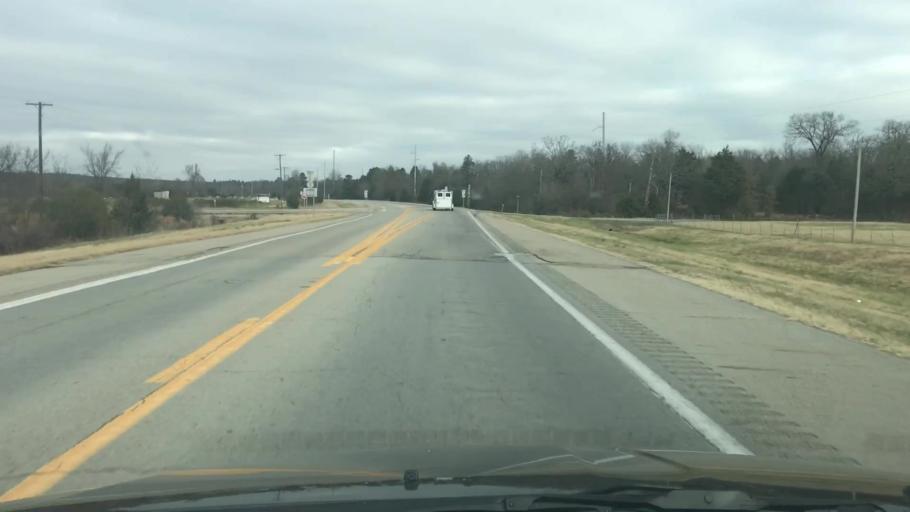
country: US
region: Arkansas
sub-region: Scott County
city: Waldron
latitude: 34.9389
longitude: -94.1022
